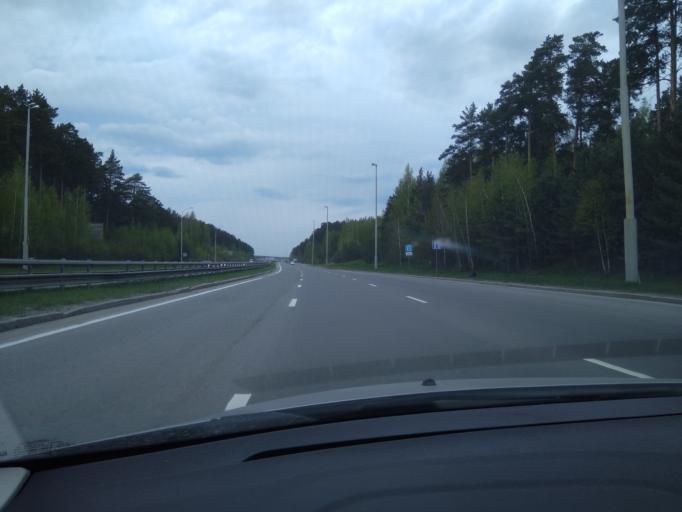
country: RU
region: Sverdlovsk
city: Yekaterinburg
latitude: 56.8875
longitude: 60.5497
